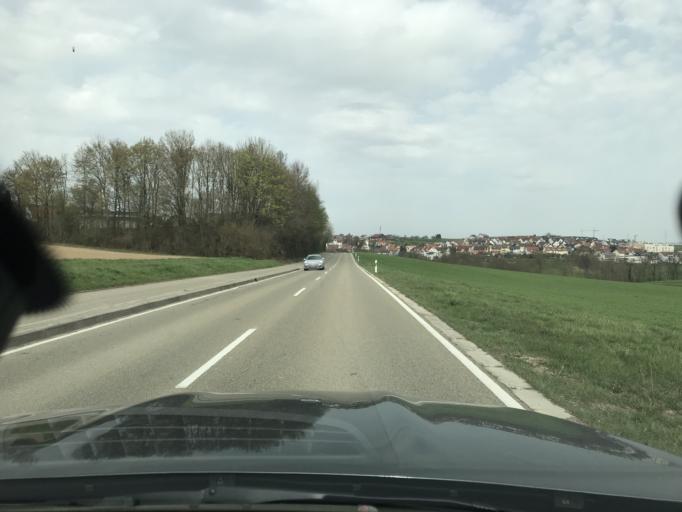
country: DE
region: Baden-Wuerttemberg
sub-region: Regierungsbezirk Stuttgart
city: Schwaikheim
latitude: 48.8945
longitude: 9.3658
